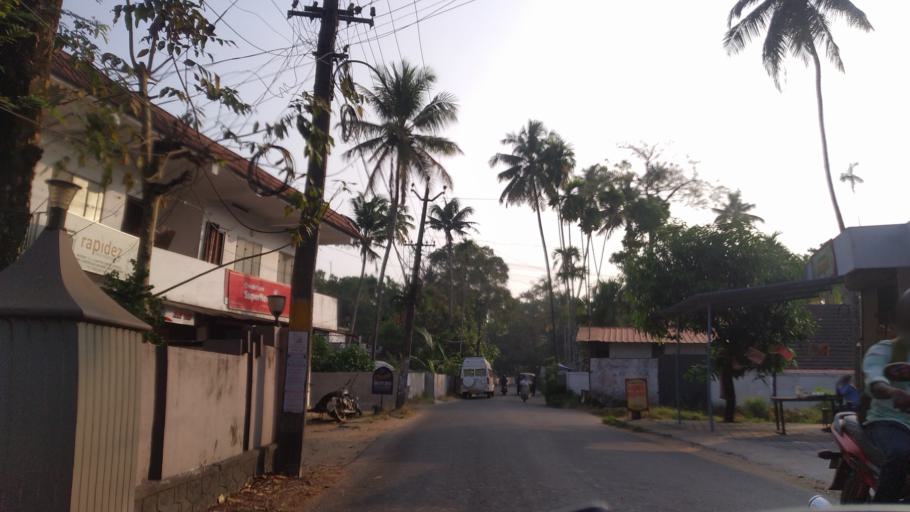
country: IN
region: Kerala
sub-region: Thrissur District
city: Kodungallur
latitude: 10.1854
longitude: 76.1957
